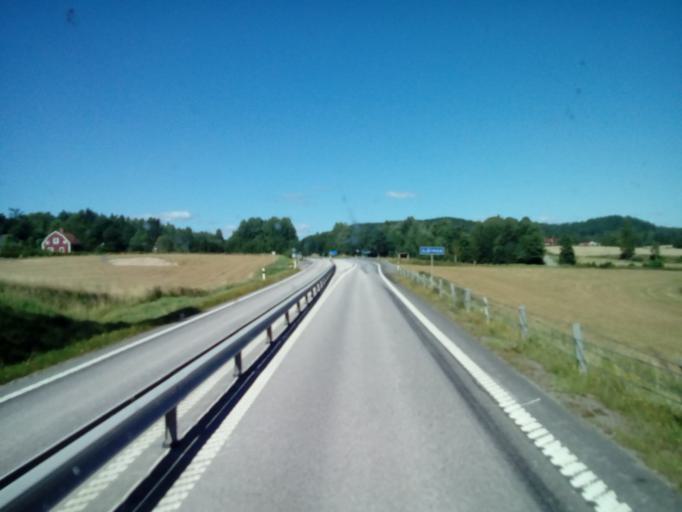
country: SE
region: OEstergoetland
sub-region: Kinda Kommun
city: Rimforsa
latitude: 58.0673
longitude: 15.6567
